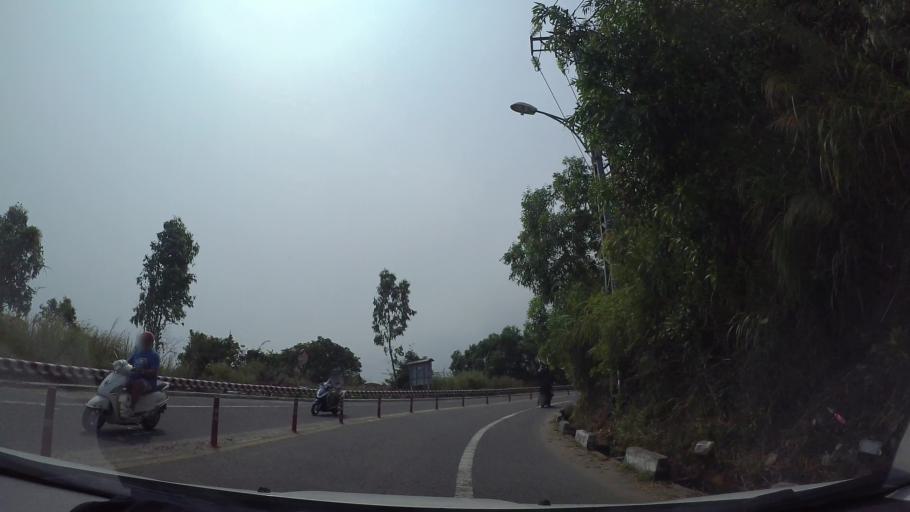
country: VN
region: Da Nang
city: Son Tra
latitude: 16.0985
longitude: 108.2768
